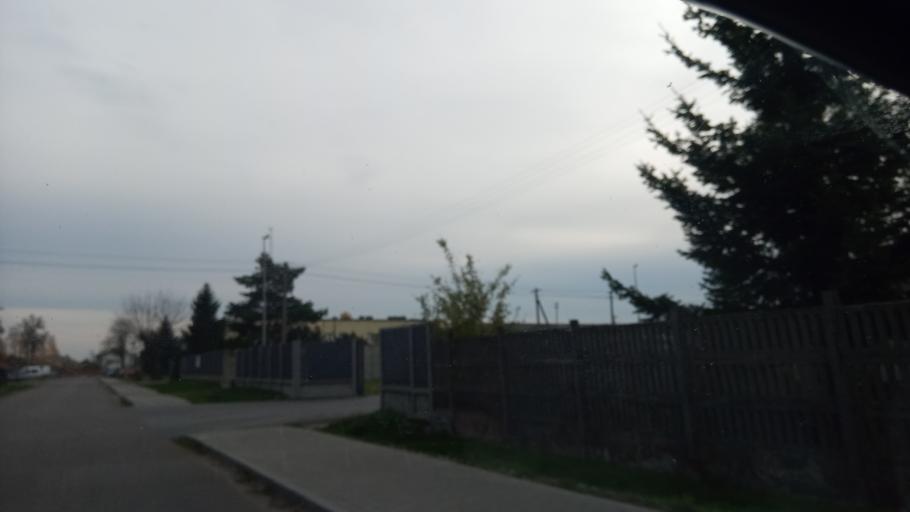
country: PL
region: Lodz Voivodeship
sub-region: Powiat skierniewicki
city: Bolimow
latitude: 52.1611
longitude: 20.1749
